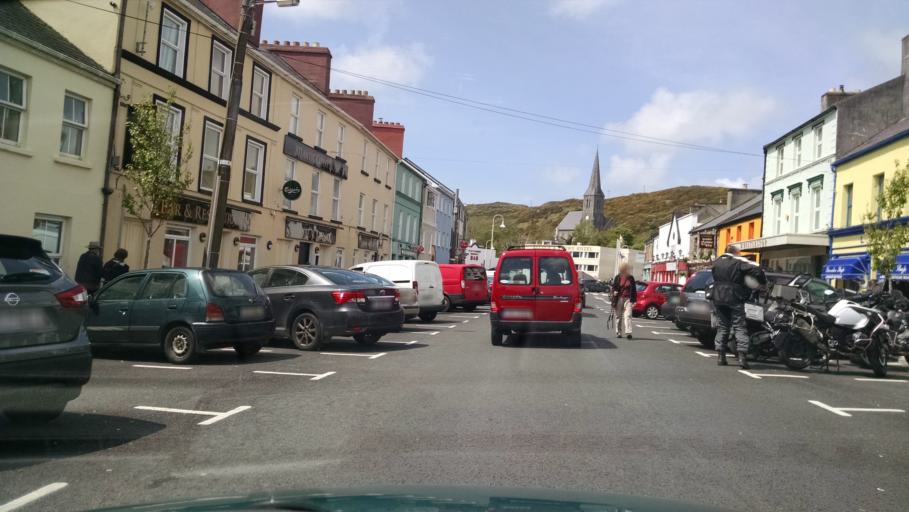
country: IE
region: Connaught
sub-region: County Galway
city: Clifden
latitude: 53.4877
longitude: -10.0212
